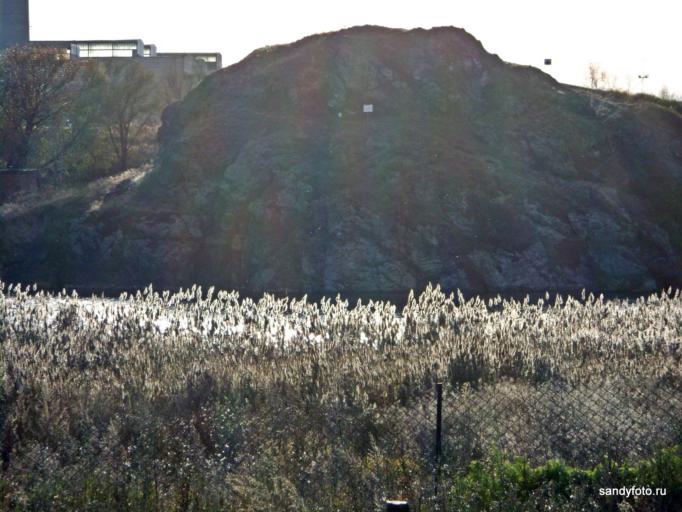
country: RU
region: Chelyabinsk
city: Troitsk
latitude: 54.0732
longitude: 61.5822
